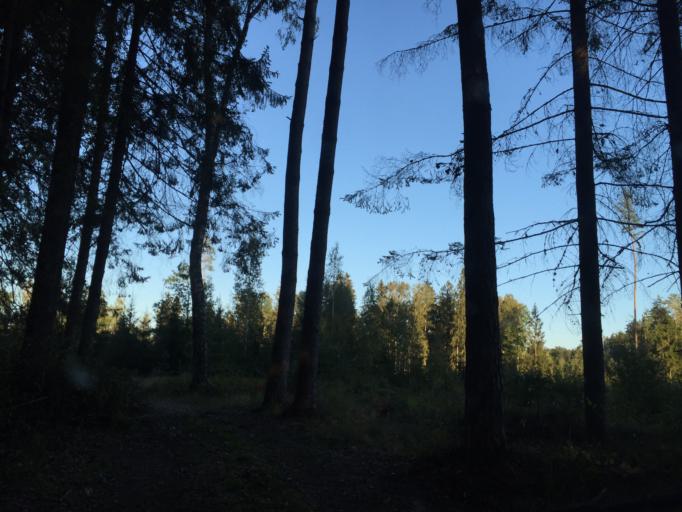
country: LV
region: Seja
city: Loja
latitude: 57.1290
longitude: 24.6221
